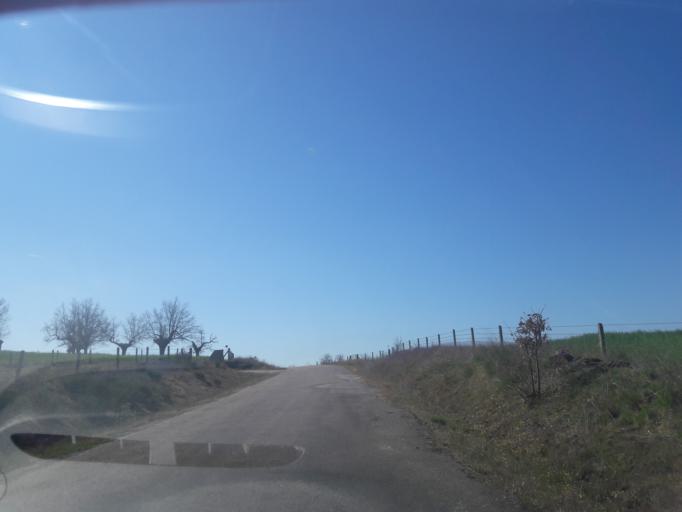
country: ES
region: Castille and Leon
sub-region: Provincia de Salamanca
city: Valsalabroso
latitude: 41.1407
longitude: -6.4847
